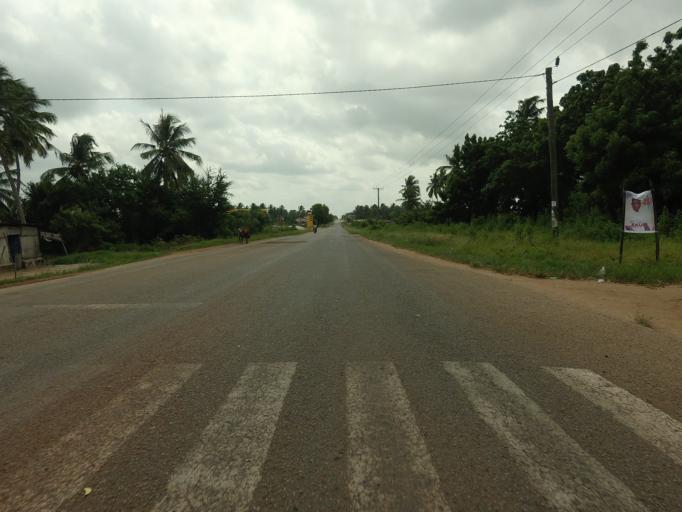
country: TG
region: Maritime
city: Lome
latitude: 6.1413
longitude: 1.1118
